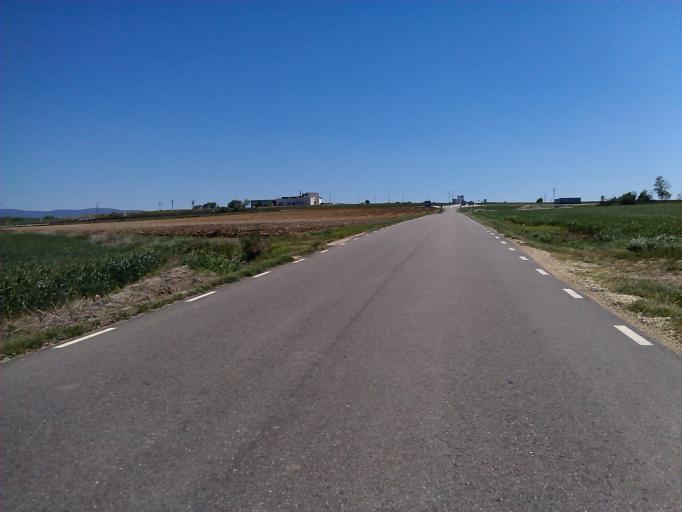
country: ES
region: Castille and Leon
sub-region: Provincia de Burgos
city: Arlanzon
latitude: 42.3542
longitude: -3.4630
